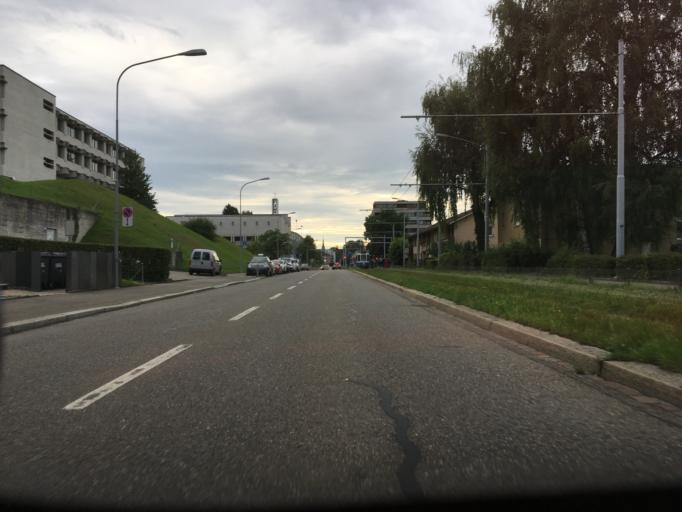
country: CH
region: Zurich
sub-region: Bezirk Zuerich
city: Zuerich (Kreis 12) / Hirzenbach
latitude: 47.4011
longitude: 8.5833
